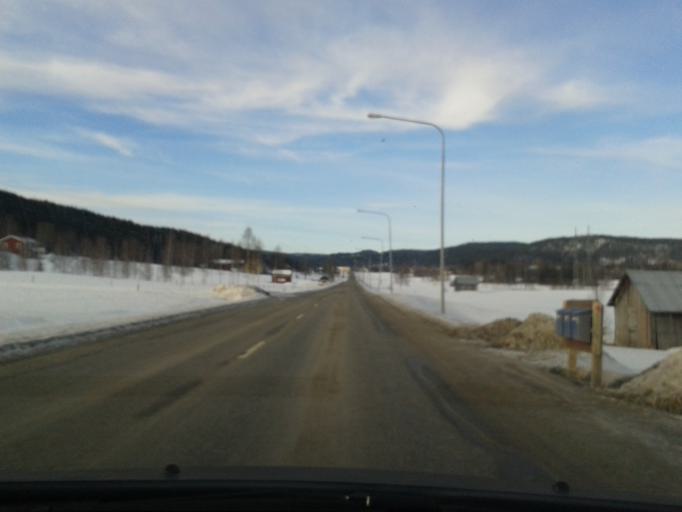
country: SE
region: Vaesternorrland
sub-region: OErnskoeldsviks Kommun
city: Bredbyn
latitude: 63.5034
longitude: 18.0754
